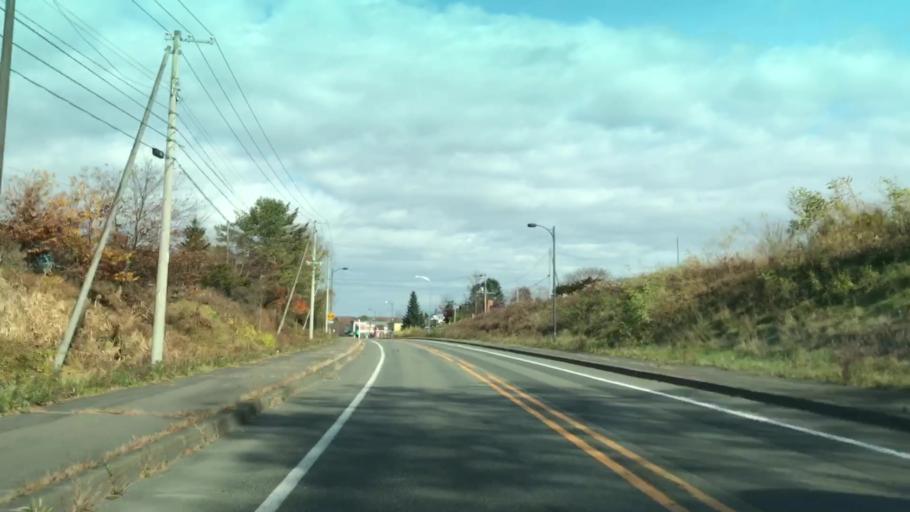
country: JP
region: Hokkaido
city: Shizunai-furukawacho
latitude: 42.6340
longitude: 142.1584
